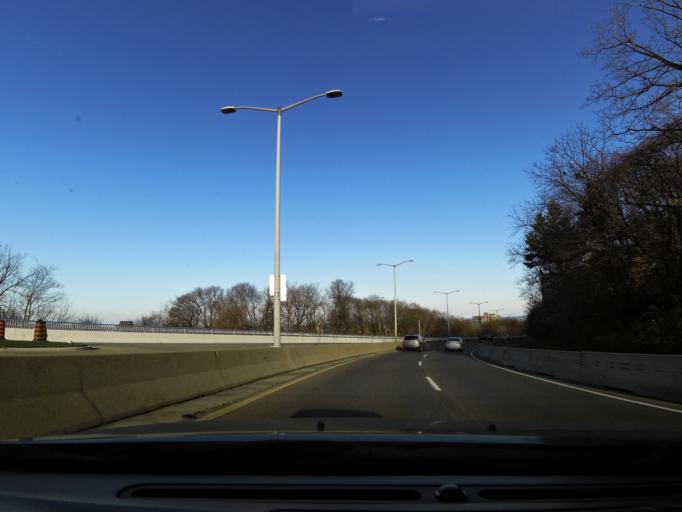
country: CA
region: Ontario
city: Hamilton
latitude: 43.2448
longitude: -79.8746
